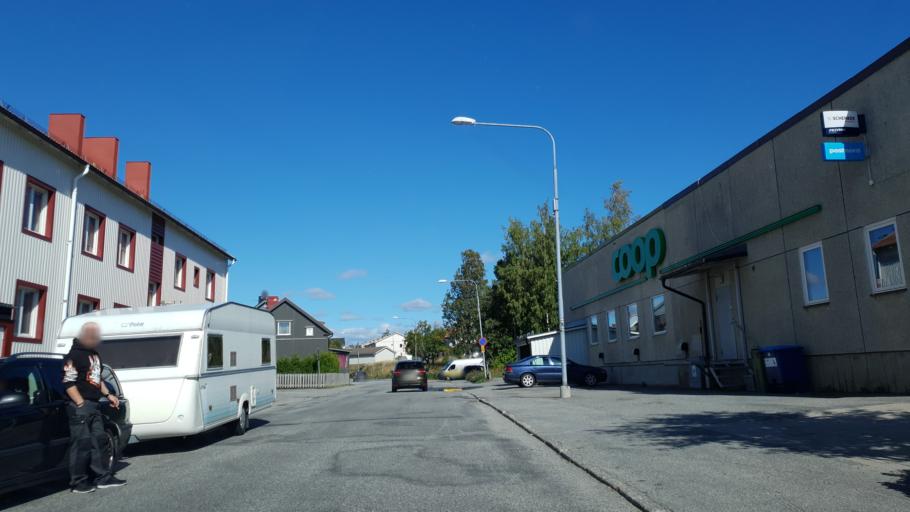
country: SE
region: Vaesterbotten
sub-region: Umea Kommun
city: Holmsund
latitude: 63.7081
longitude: 20.3639
